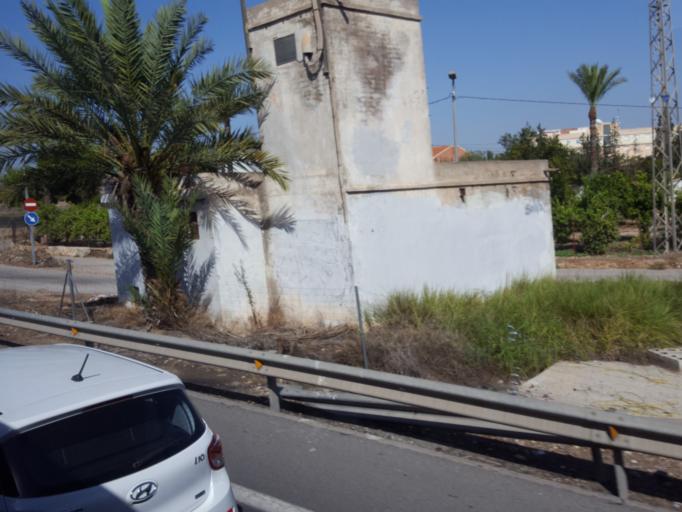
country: ES
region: Murcia
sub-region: Murcia
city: Murcia
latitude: 38.0030
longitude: -1.1632
